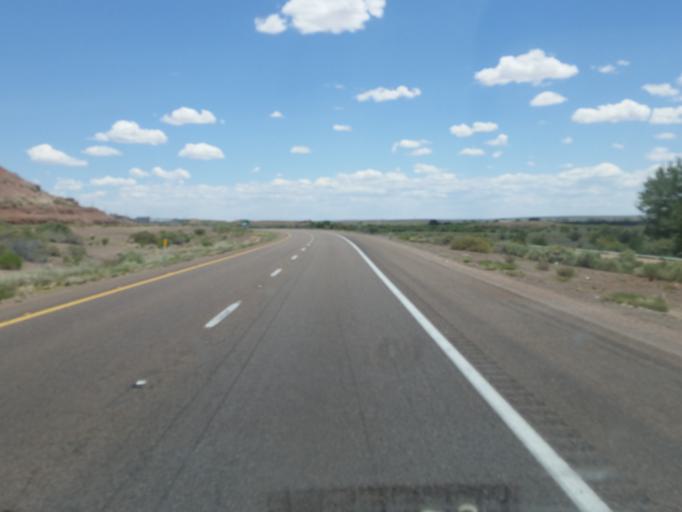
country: US
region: Arizona
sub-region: Navajo County
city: Joseph City
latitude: 34.9330
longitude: -110.2745
